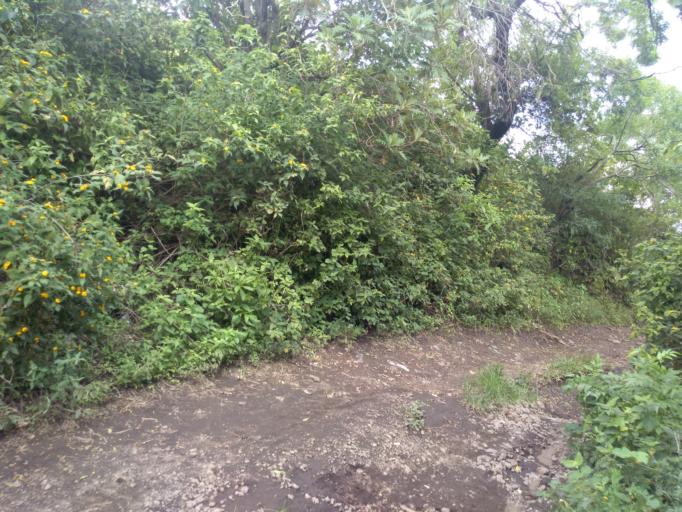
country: GT
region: Escuintla
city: San Vicente Pacaya
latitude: 14.3702
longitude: -90.5694
